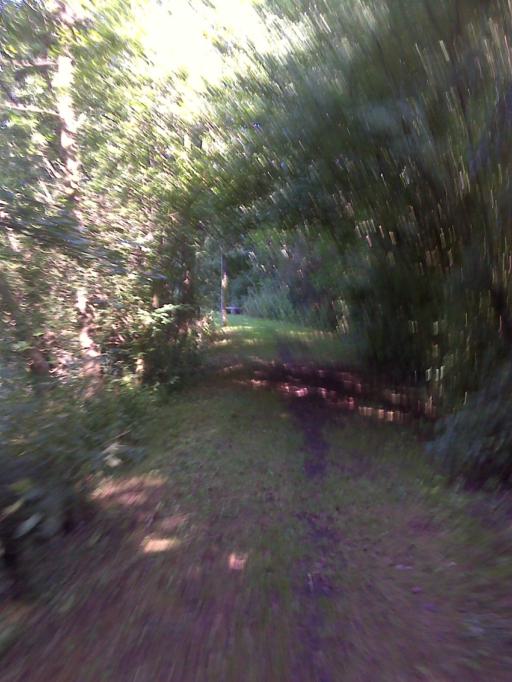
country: FR
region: Nord-Pas-de-Calais
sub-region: Departement du Nord
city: Leval
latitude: 50.1799
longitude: 3.8237
